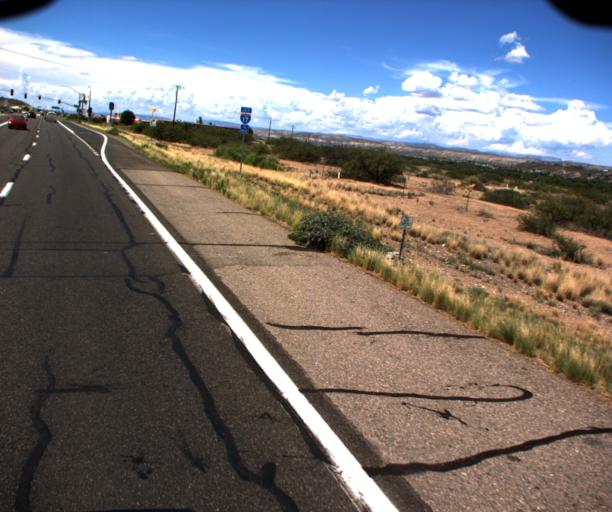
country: US
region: Arizona
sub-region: Yavapai County
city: Camp Verde
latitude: 34.5710
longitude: -111.8797
